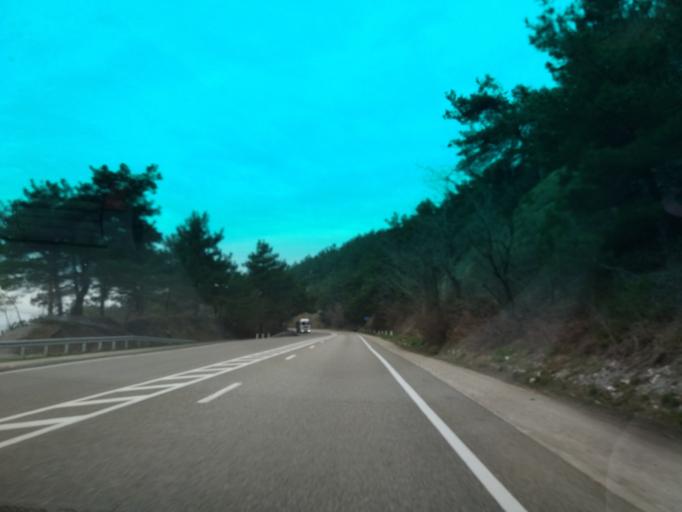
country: RU
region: Krasnodarskiy
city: Ol'ginka
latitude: 44.1873
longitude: 38.9105
